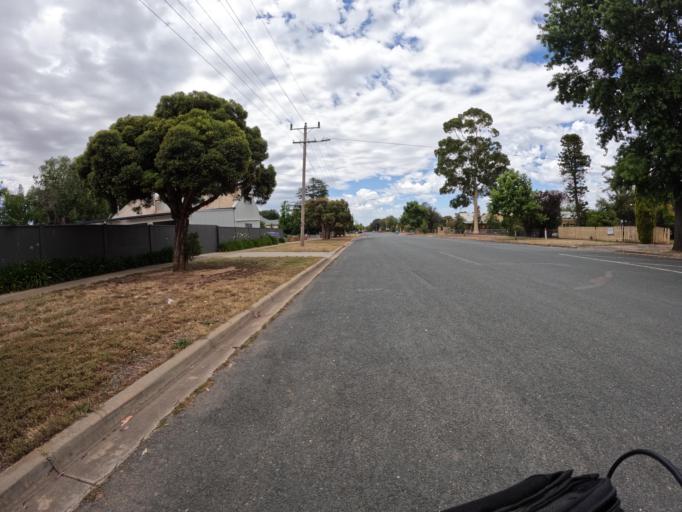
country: AU
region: Victoria
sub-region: Greater Shepparton
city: Shepparton
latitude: -36.6163
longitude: 145.2155
